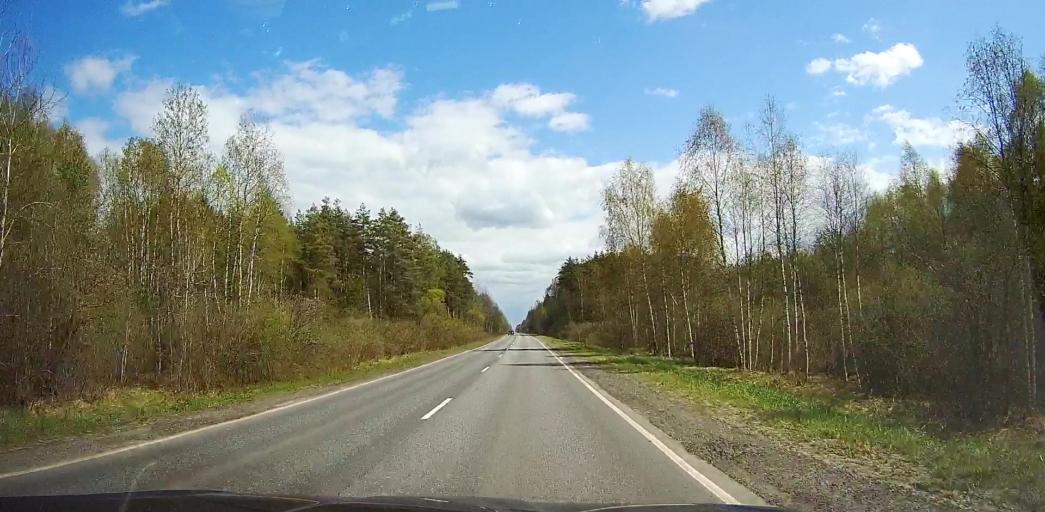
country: RU
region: Moskovskaya
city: Imeni Tsyurupy
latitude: 55.5515
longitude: 38.7205
